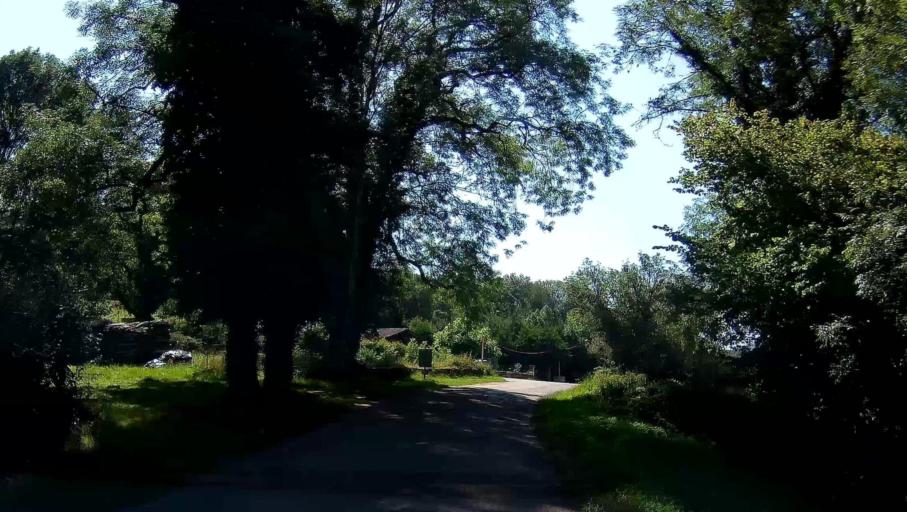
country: FR
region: Bourgogne
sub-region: Departement de la Cote-d'Or
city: Nolay
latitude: 46.9786
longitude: 4.6447
